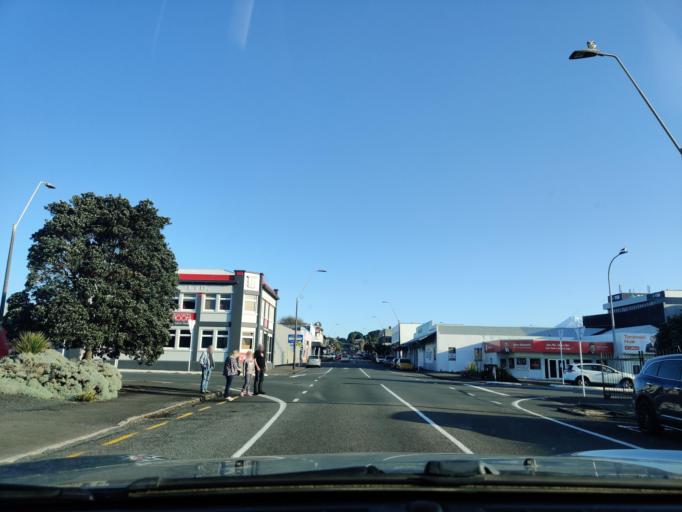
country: NZ
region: Taranaki
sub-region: New Plymouth District
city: New Plymouth
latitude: -39.0551
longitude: 174.0784
